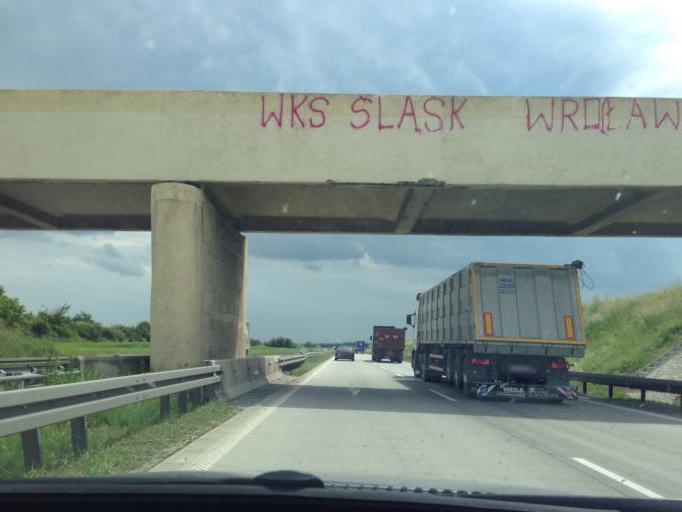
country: PL
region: Lower Silesian Voivodeship
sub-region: Powiat sredzki
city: Udanin
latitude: 51.1161
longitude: 16.3829
